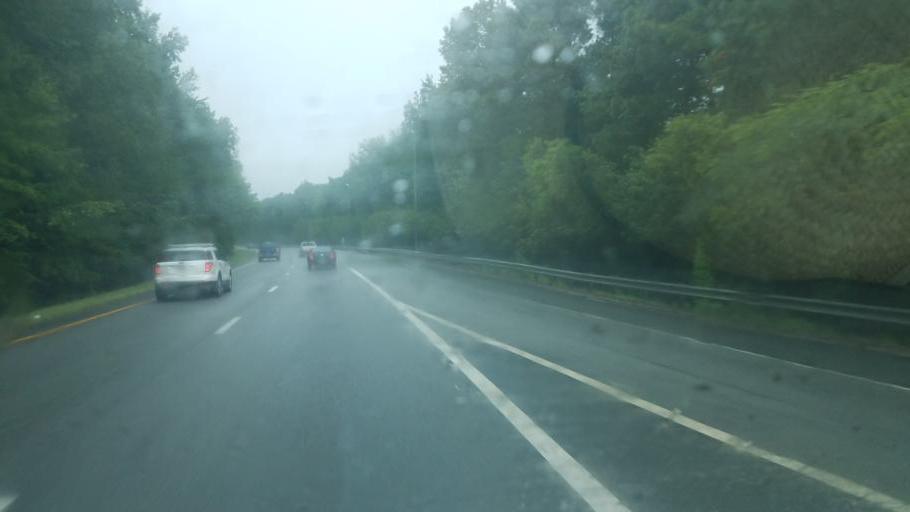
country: US
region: Virginia
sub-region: City of Portsmouth
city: Portsmouth Heights
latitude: 36.7742
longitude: -76.3679
